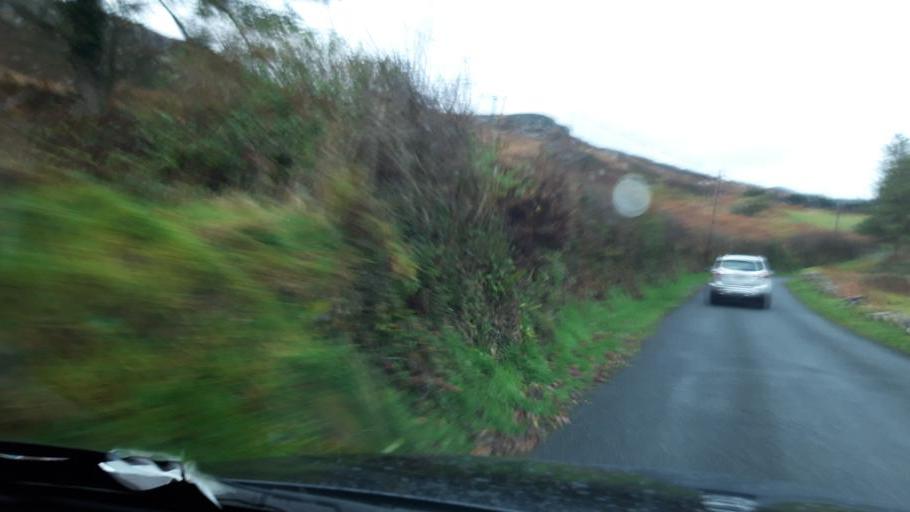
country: IE
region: Ulster
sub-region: County Donegal
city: Buncrana
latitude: 55.2362
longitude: -7.6183
